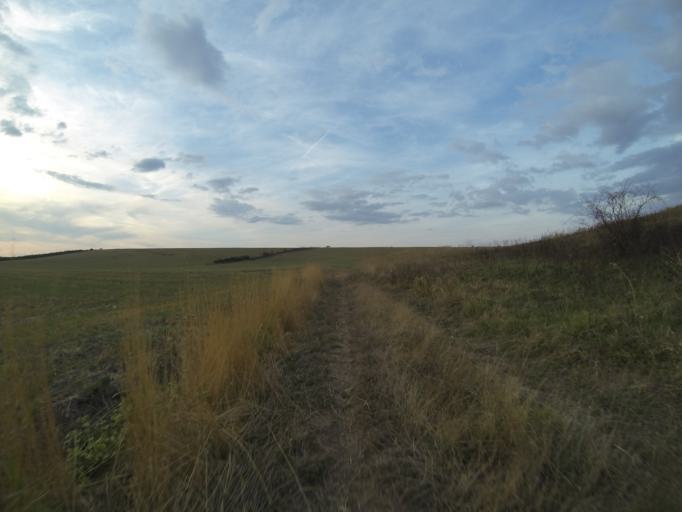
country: RO
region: Dolj
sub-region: Comuna Ceratu
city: Ceratu
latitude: 44.0957
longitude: 23.6652
